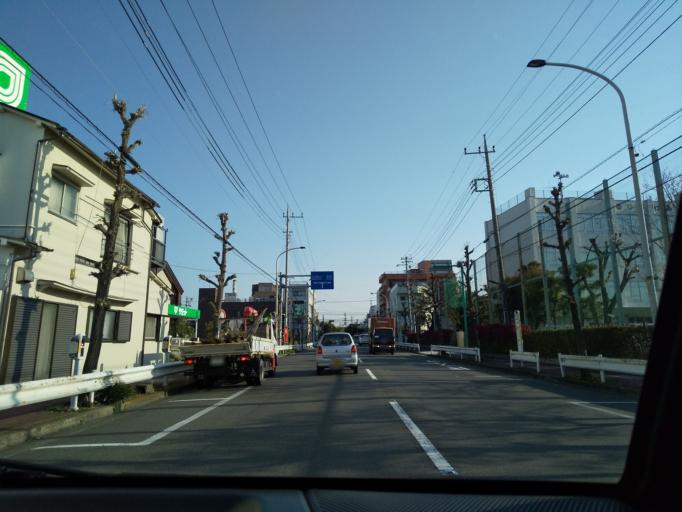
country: JP
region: Tokyo
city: Hino
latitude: 35.6950
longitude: 139.4261
